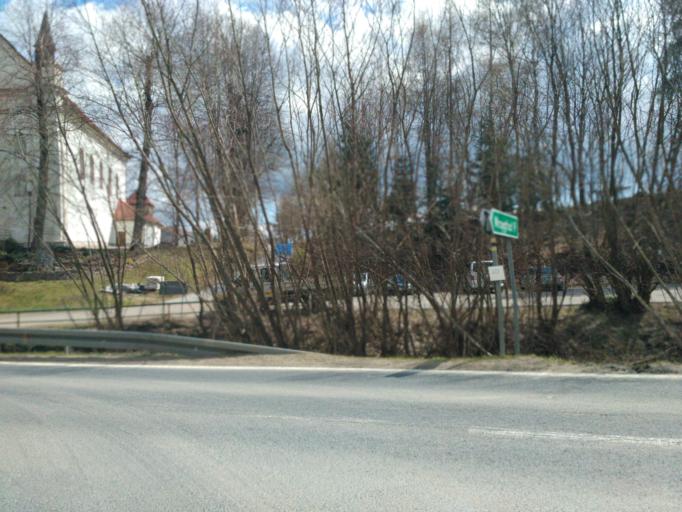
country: PL
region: Subcarpathian Voivodeship
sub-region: Powiat sanocki
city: Tyrawa Woloska
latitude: 49.5765
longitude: 22.3643
